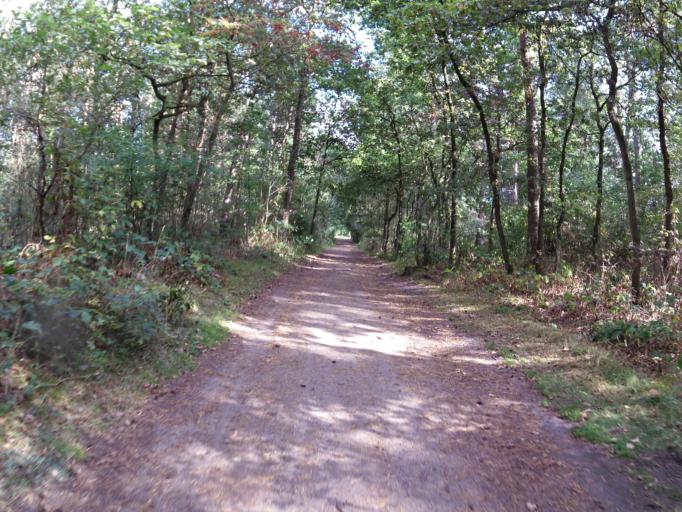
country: DE
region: Lower Saxony
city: Hamersen
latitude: 53.2757
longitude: 9.4782
